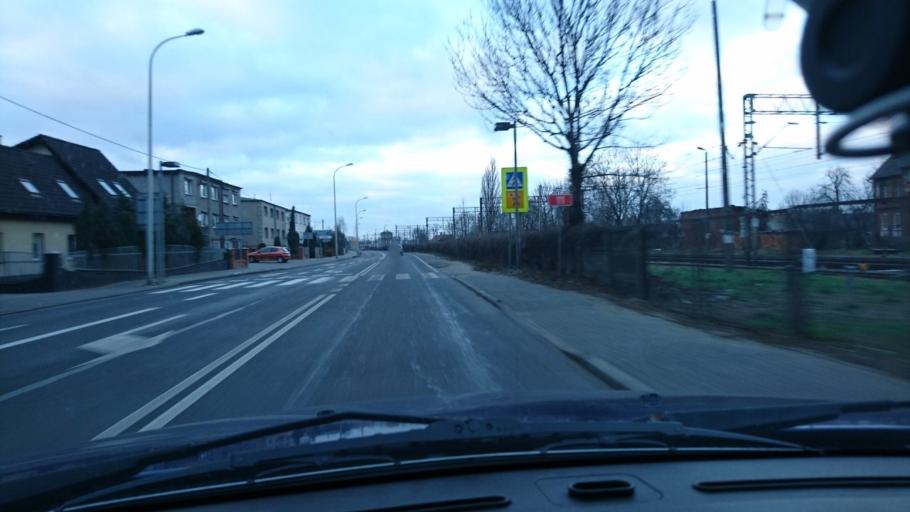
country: PL
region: Greater Poland Voivodeship
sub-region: Powiat kepinski
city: Kepno
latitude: 51.2981
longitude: 17.9971
